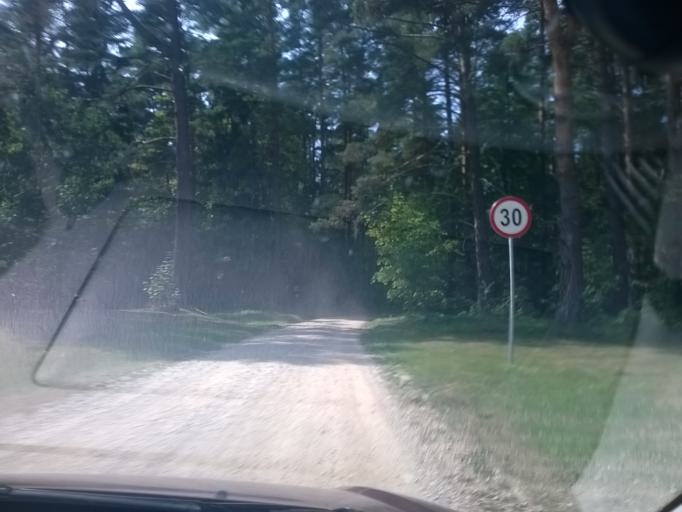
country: EE
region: Tartu
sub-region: Puhja vald
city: Puhja
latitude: 58.2518
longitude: 26.1766
